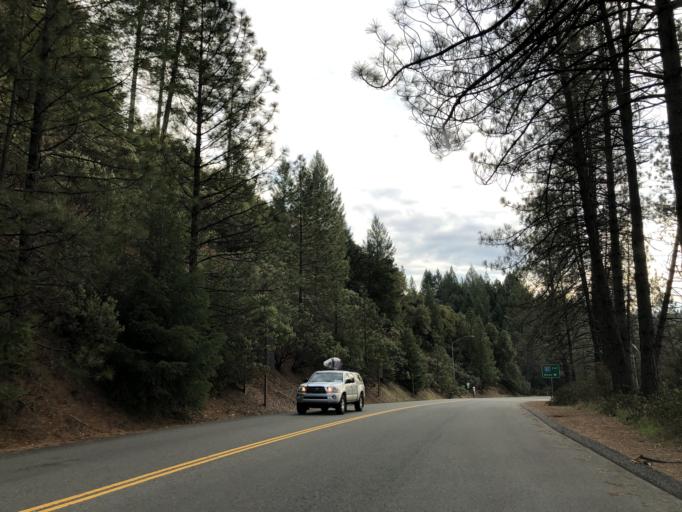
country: US
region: California
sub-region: Placer County
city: Colfax
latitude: 39.0782
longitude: -120.9592
